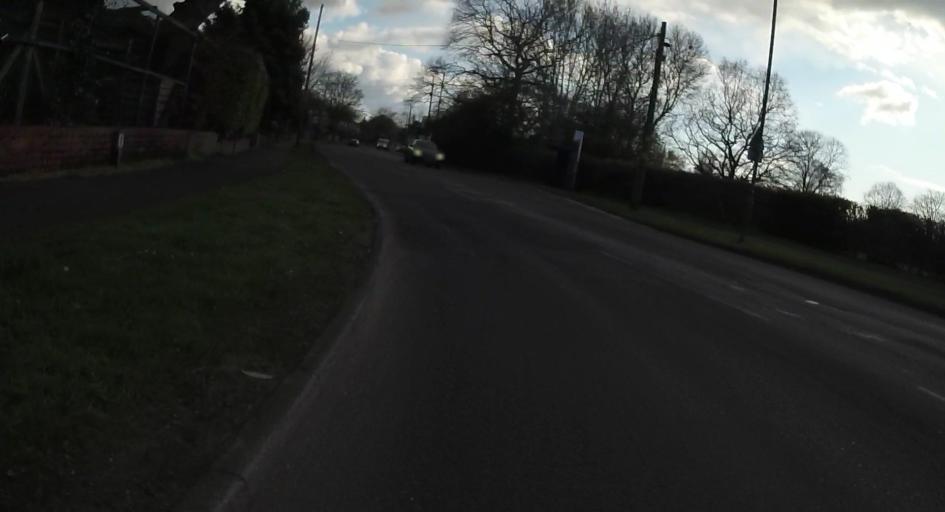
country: GB
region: England
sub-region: Hampshire
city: Farnborough
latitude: 51.3041
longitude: -0.7595
